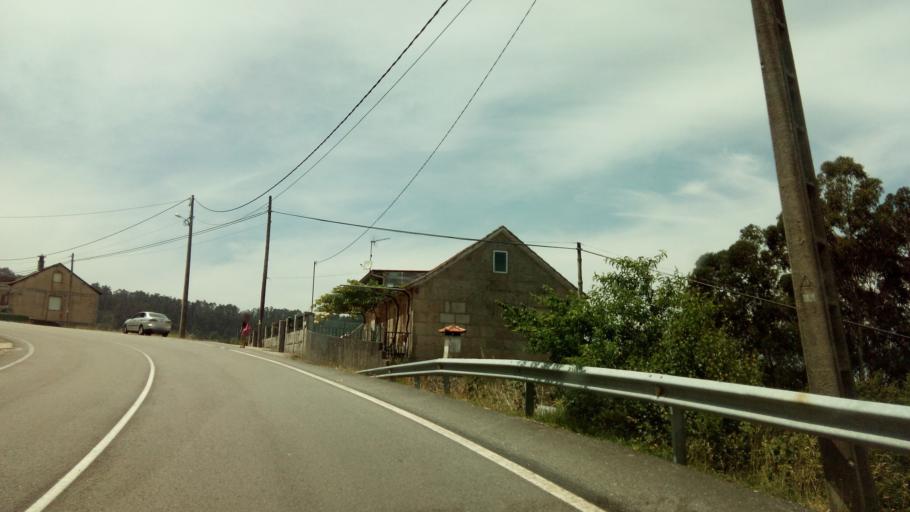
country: ES
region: Galicia
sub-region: Provincia de Pontevedra
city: Marin
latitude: 42.3493
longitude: -8.7010
